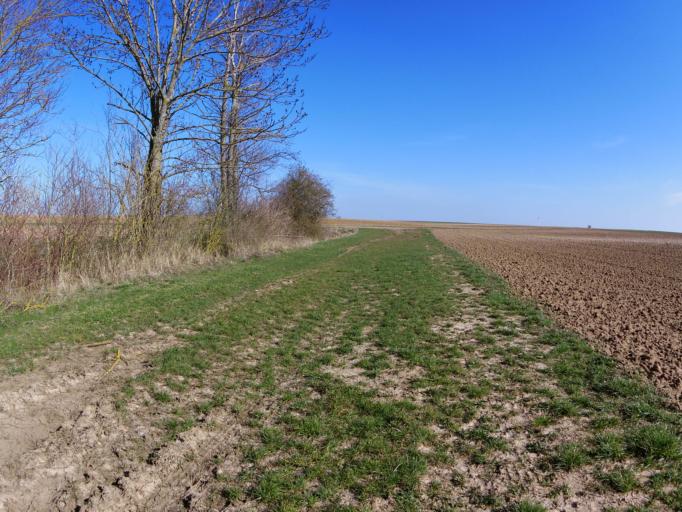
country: DE
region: Bavaria
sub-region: Regierungsbezirk Unterfranken
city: Prosselsheim
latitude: 49.8571
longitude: 10.1112
